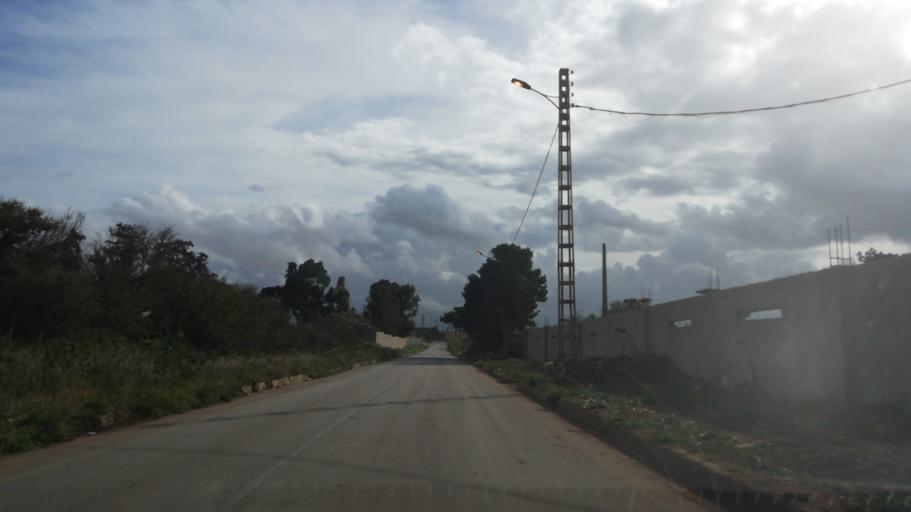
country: DZ
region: Oran
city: Es Senia
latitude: 35.6568
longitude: -0.6376
